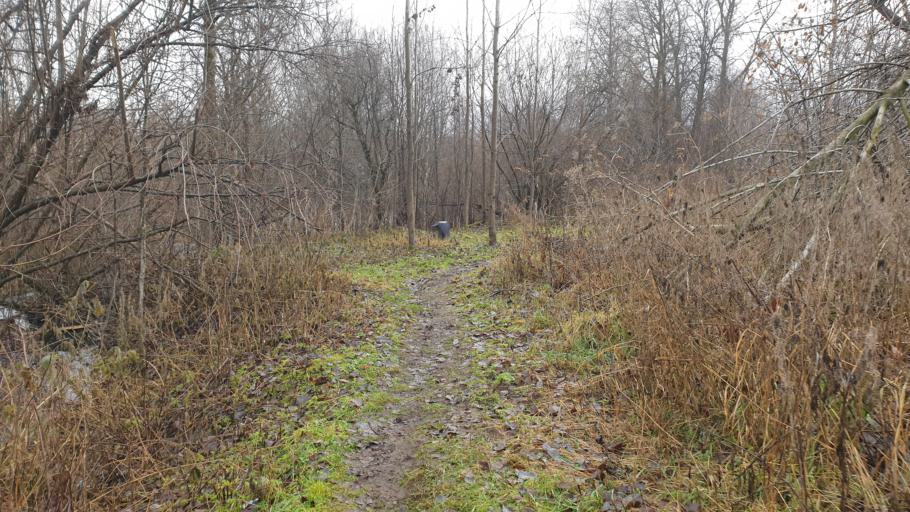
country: RU
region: Kirov
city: Kirs
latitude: 59.3353
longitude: 52.2403
